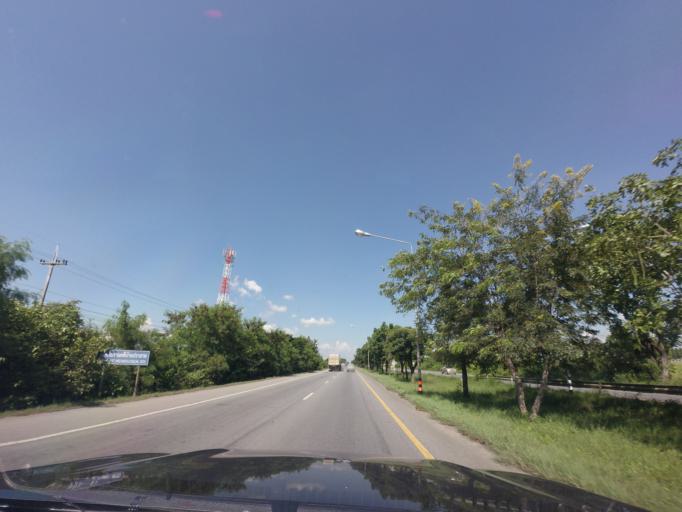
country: TH
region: Nakhon Ratchasima
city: Non Sung
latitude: 15.2238
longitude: 102.3641
